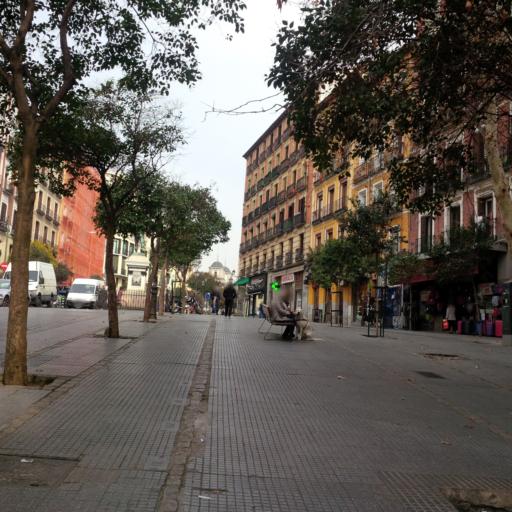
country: ES
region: Madrid
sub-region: Provincia de Madrid
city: Madrid
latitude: 40.4099
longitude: -3.7072
